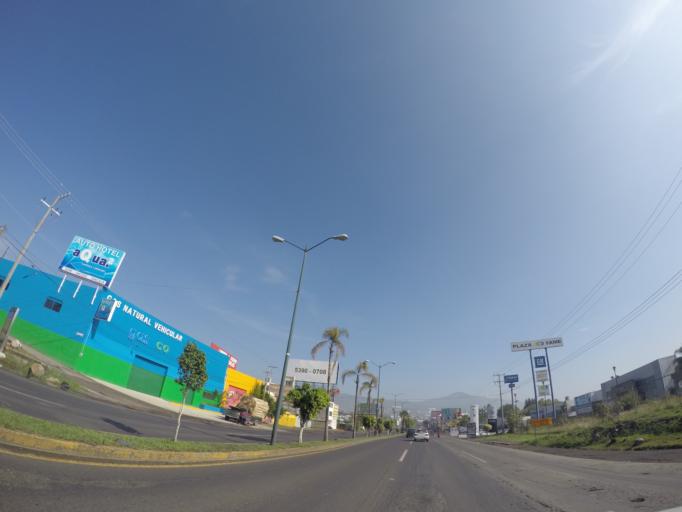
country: MX
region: Michoacan
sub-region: Morelia
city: San Antonio
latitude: 19.6900
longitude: -101.2391
